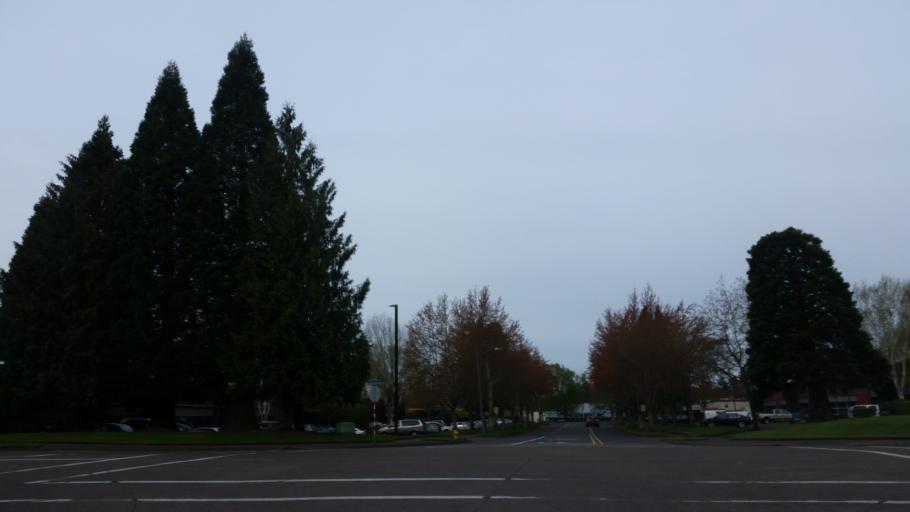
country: US
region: Oregon
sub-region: Washington County
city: Durham
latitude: 45.4118
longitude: -122.7467
